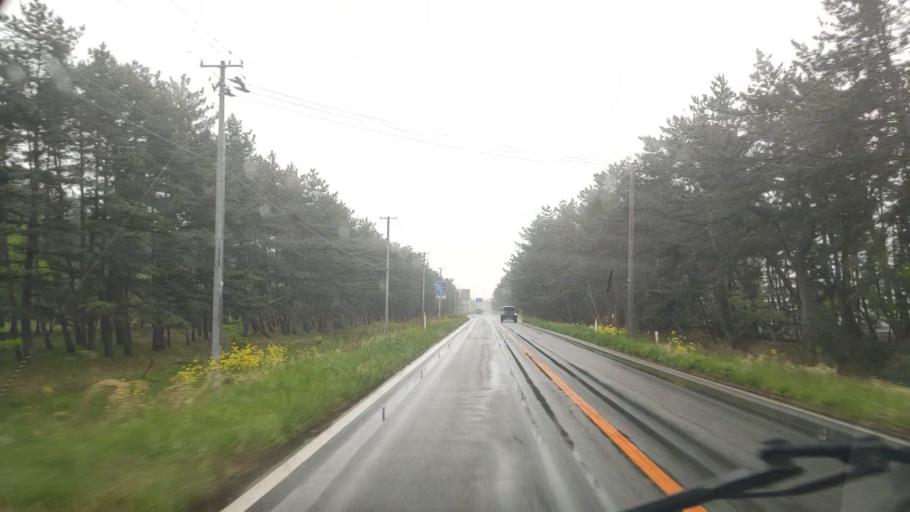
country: JP
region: Akita
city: Tenno
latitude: 40.0213
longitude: 139.9527
